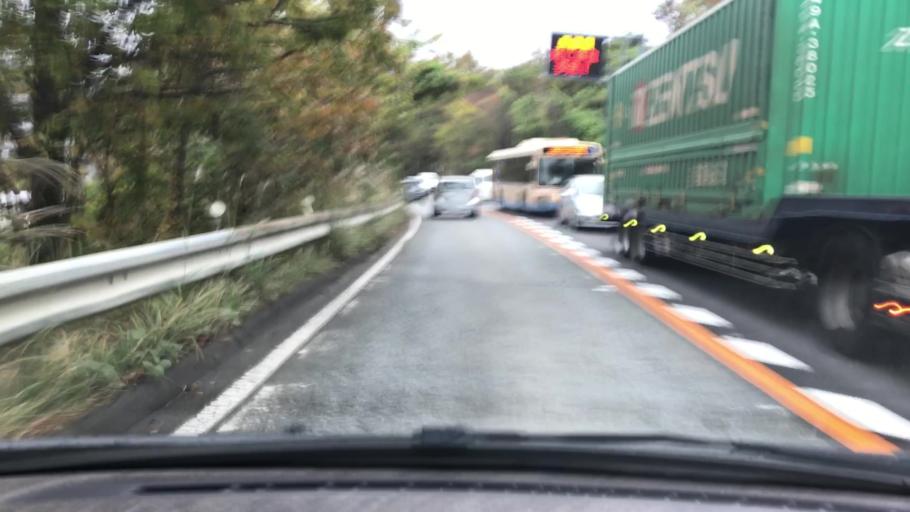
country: JP
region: Hyogo
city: Takarazuka
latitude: 34.8309
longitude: 135.2866
